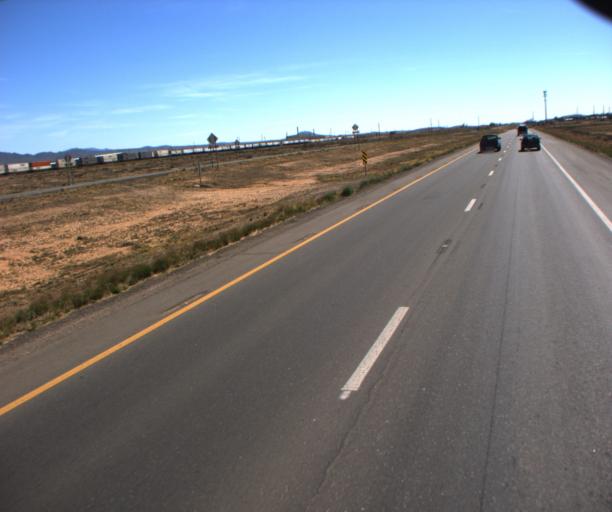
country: US
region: Arizona
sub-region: Mohave County
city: New Kingman-Butler
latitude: 35.2702
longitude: -113.9602
